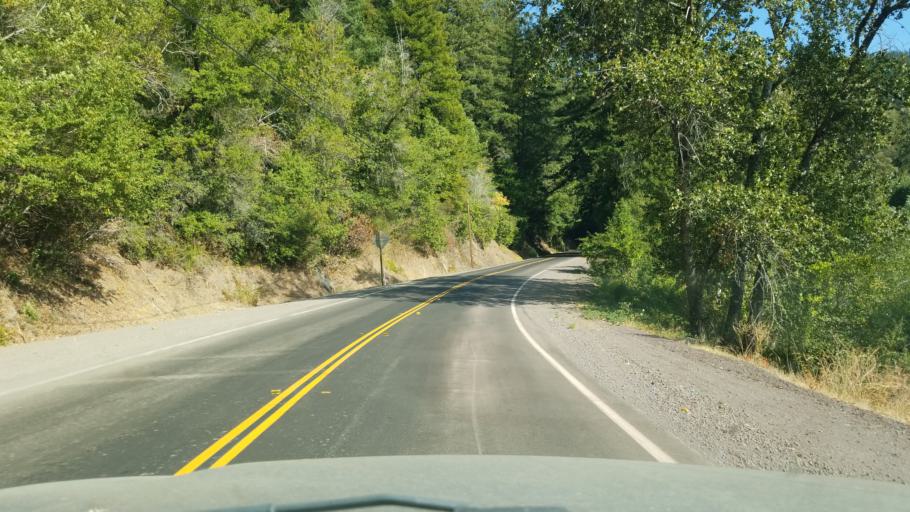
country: US
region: California
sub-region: Humboldt County
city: Redway
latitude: 40.2224
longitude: -123.7896
